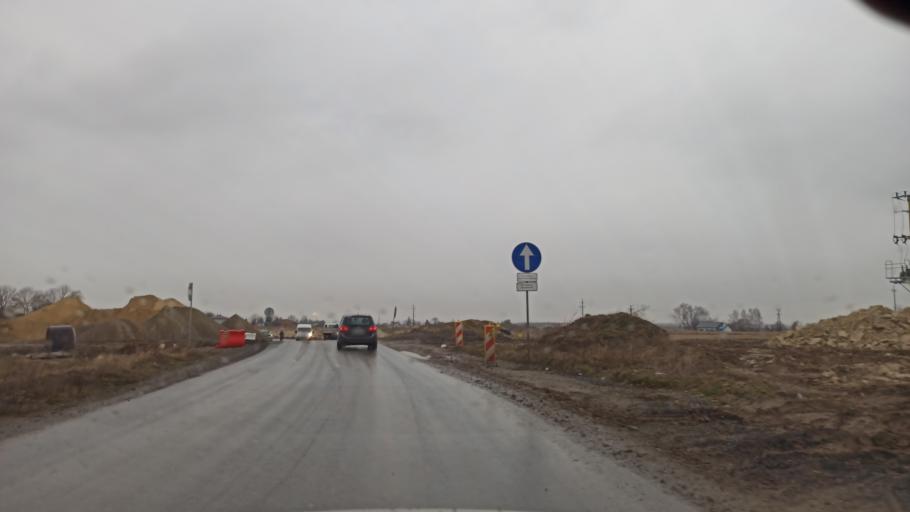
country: PL
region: Lublin Voivodeship
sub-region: Powiat lubelski
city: Niedrzwica Duza
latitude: 51.1019
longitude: 22.4078
